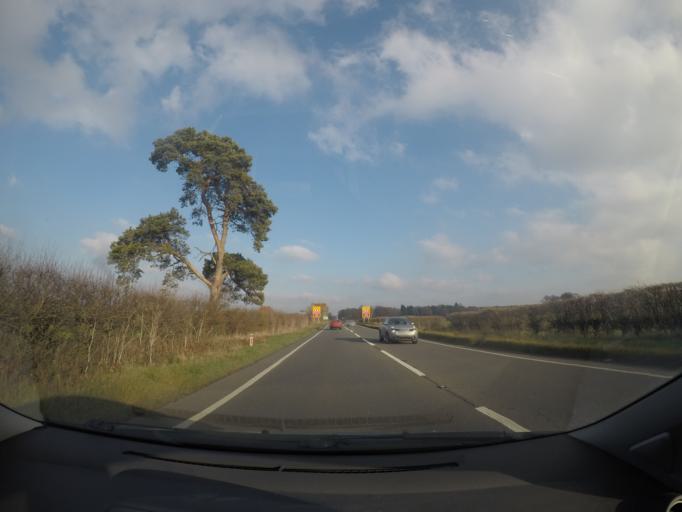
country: GB
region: England
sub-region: City of York
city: Holtby
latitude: 54.0104
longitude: -0.9958
